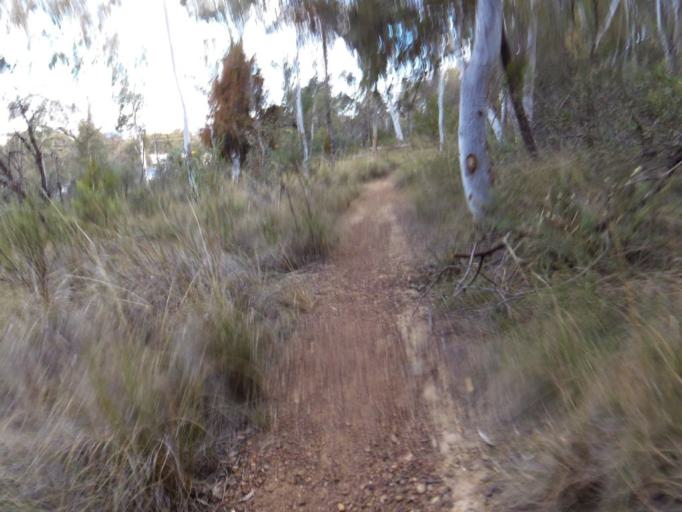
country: AU
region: Australian Capital Territory
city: Acton
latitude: -35.2637
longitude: 149.1112
